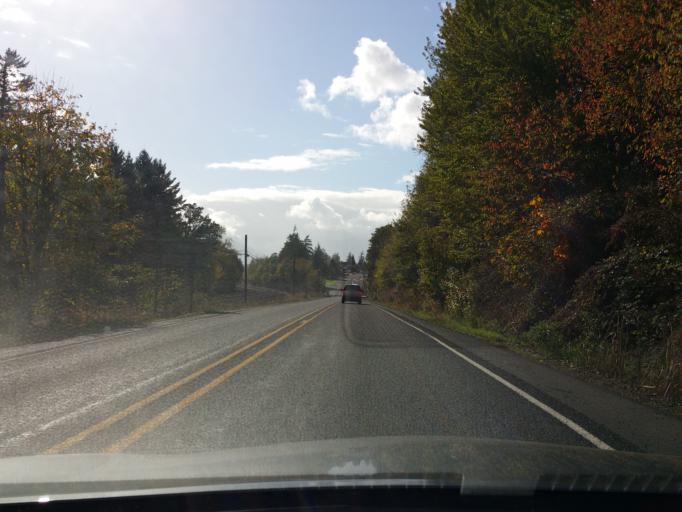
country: US
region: Washington
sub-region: Skamania County
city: Stevenson
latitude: 45.6992
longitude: -121.8733
